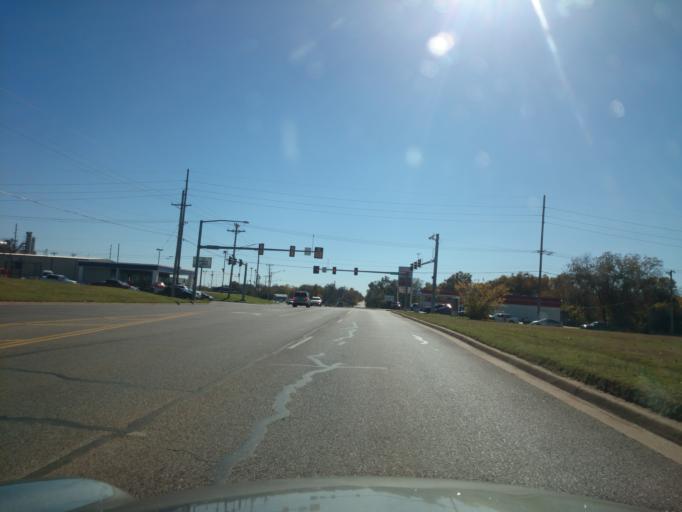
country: US
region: Oklahoma
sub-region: Payne County
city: Stillwater
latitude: 36.1458
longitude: -97.0697
